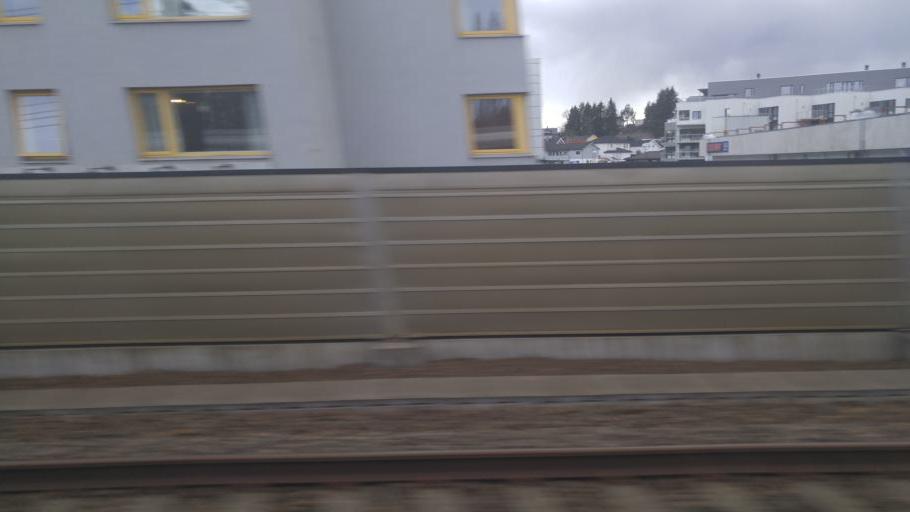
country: NO
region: Akershus
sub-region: Skedsmo
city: Lillestrom
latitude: 59.9633
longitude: 11.0654
